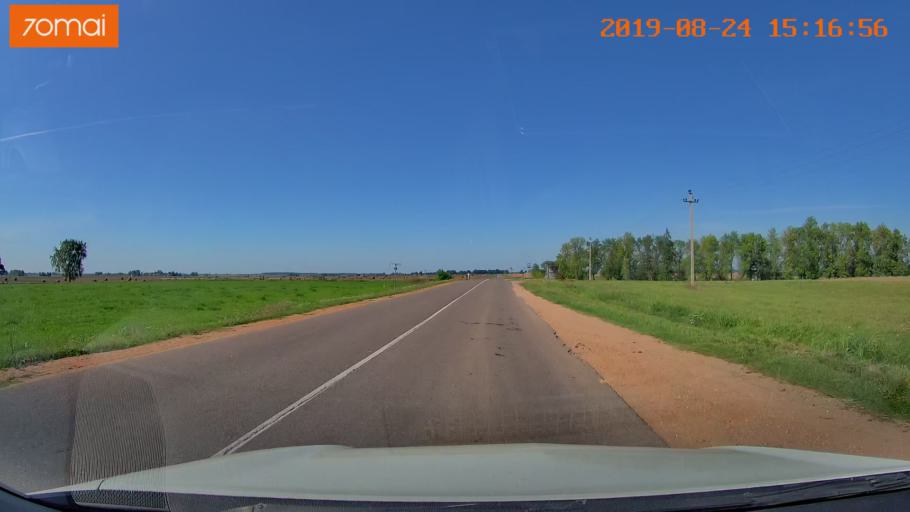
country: BY
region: Minsk
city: Samakhvalavichy
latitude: 53.6459
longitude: 27.5487
